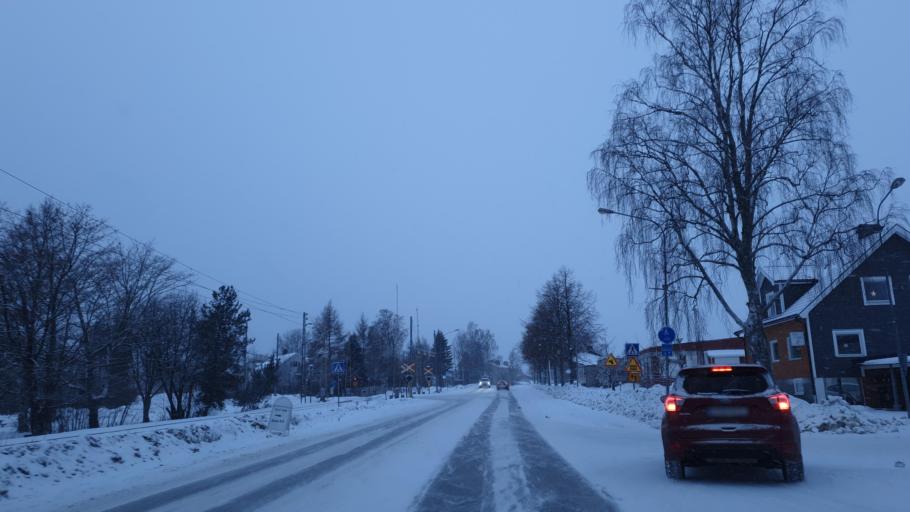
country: SE
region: Vaesternorrland
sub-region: OErnskoeldsviks Kommun
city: Ornskoldsvik
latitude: 63.2952
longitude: 18.6233
